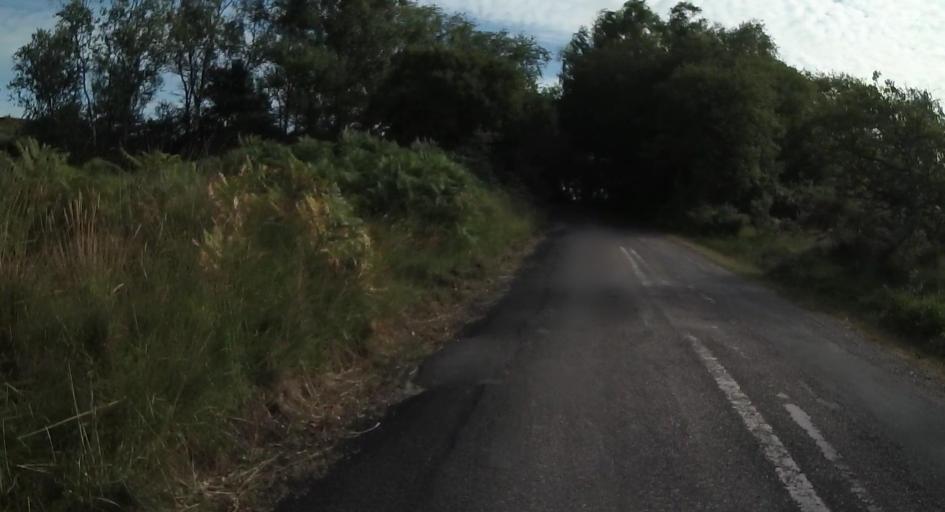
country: GB
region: England
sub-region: Dorset
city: Wareham
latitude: 50.6767
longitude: -2.0774
